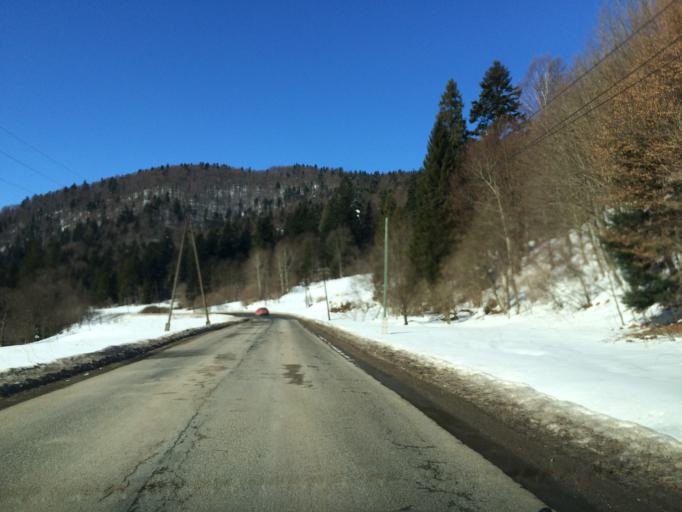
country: PL
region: Subcarpathian Voivodeship
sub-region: Powiat leski
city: Cisna
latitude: 49.2078
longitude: 22.3187
